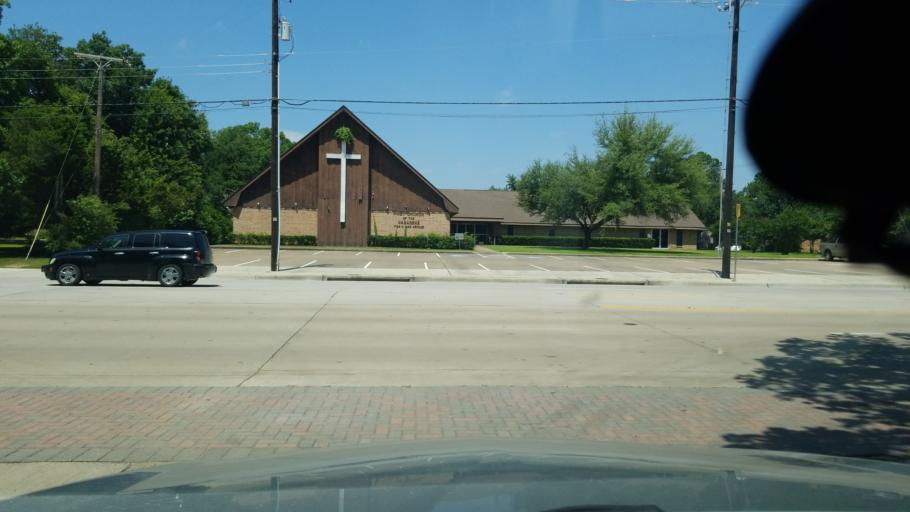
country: US
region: Texas
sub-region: Dallas County
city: Irving
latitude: 32.8319
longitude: -96.9589
